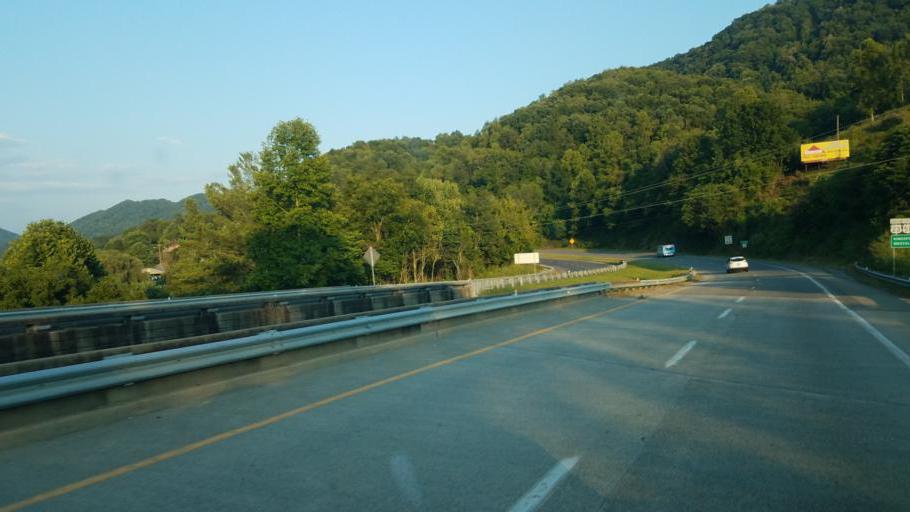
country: US
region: Virginia
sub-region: Scott County
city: Gate City
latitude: 36.6322
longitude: -82.6119
